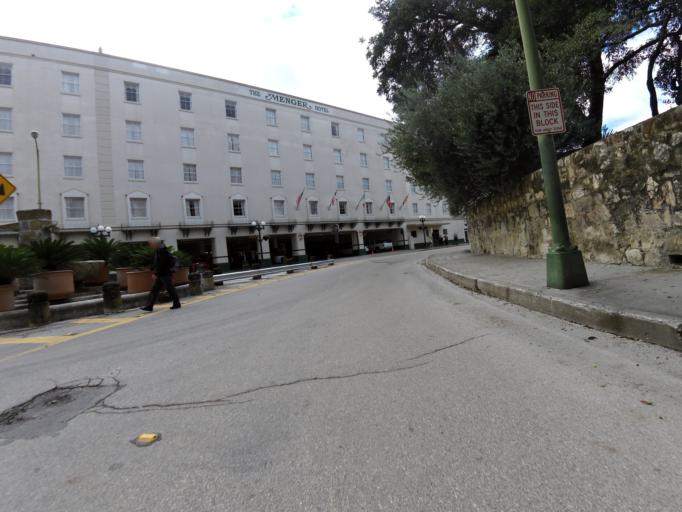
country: US
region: Texas
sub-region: Bexar County
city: San Antonio
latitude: 29.4253
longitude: -98.4854
